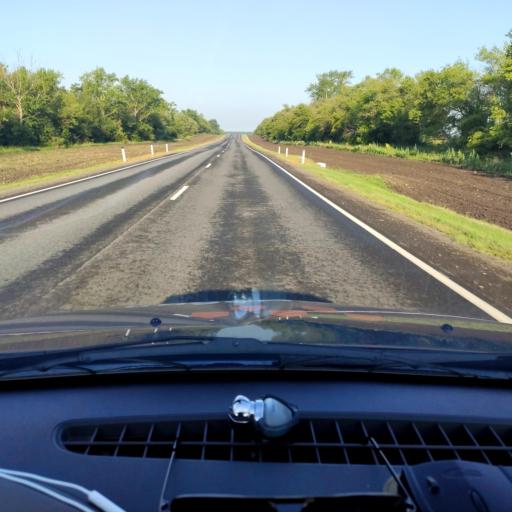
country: RU
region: Orjol
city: Livny
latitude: 52.4304
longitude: 37.7957
